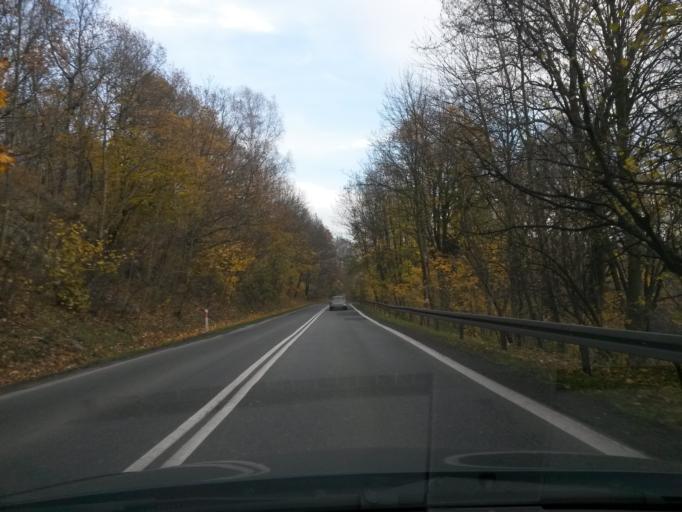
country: PL
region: Lower Silesian Voivodeship
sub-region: Powiat jaworski
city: Bolkow
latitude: 50.9245
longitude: 16.0900
